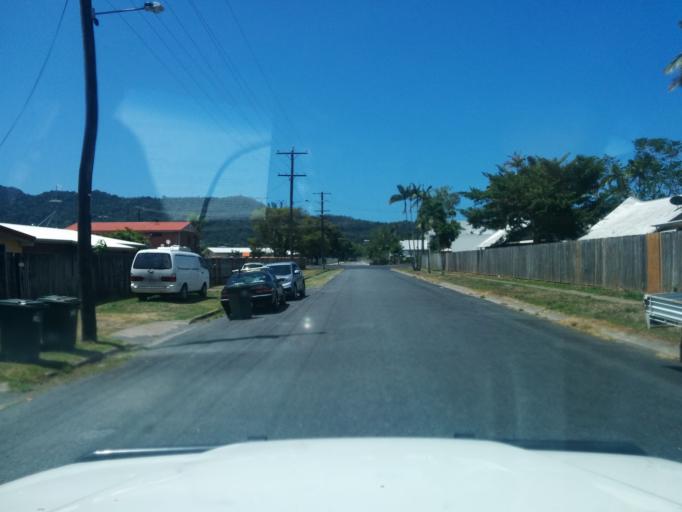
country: AU
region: Queensland
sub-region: Cairns
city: Cairns
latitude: -16.9131
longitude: 145.7474
